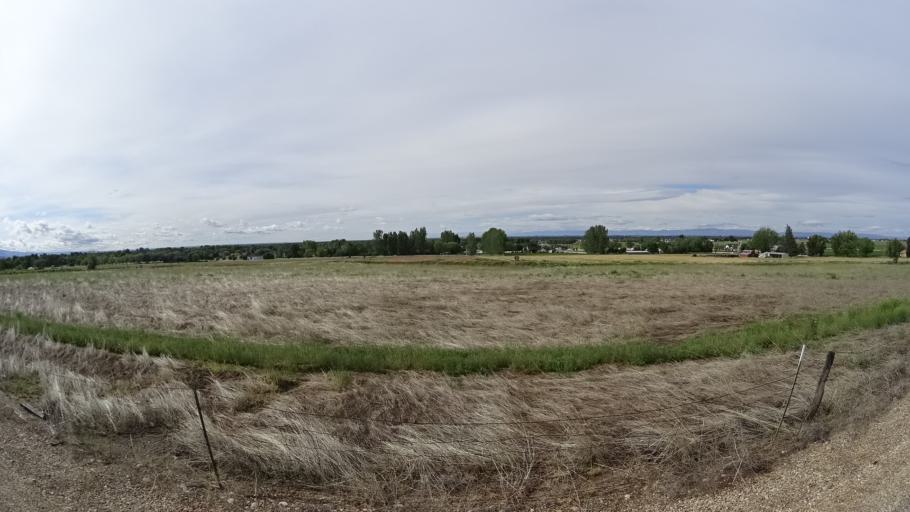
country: US
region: Idaho
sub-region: Ada County
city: Eagle
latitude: 43.7358
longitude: -116.4094
